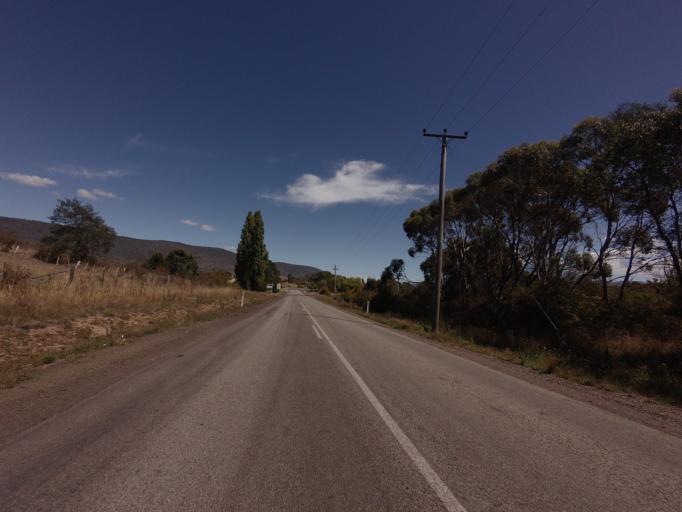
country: AU
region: Tasmania
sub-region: Break O'Day
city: St Helens
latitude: -41.6339
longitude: 147.9829
